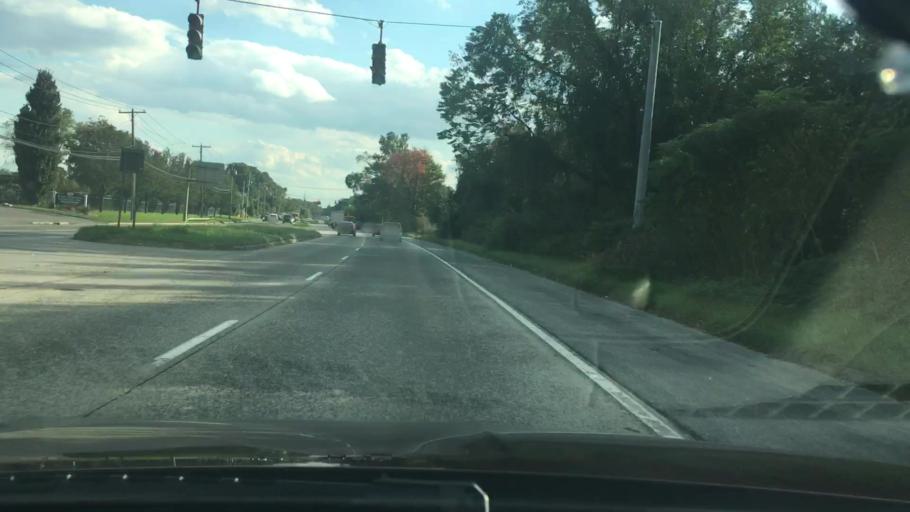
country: US
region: New York
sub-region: Suffolk County
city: Dix Hills
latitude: 40.7907
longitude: -73.3413
